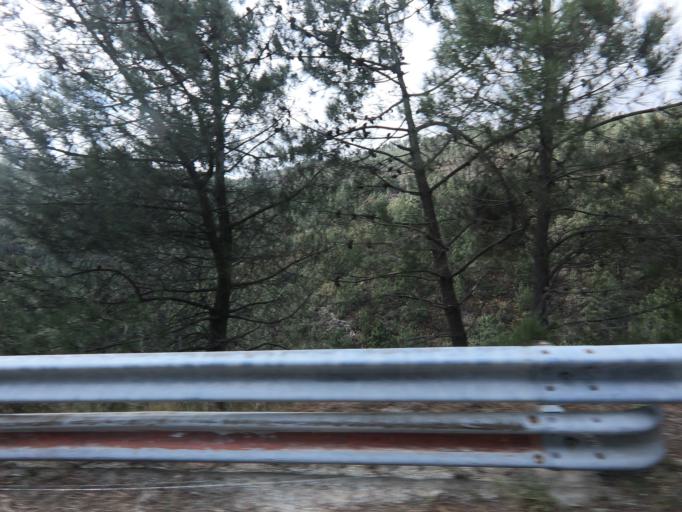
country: PT
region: Vila Real
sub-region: Vila Real
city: Vila Real
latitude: 41.3361
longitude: -7.7791
